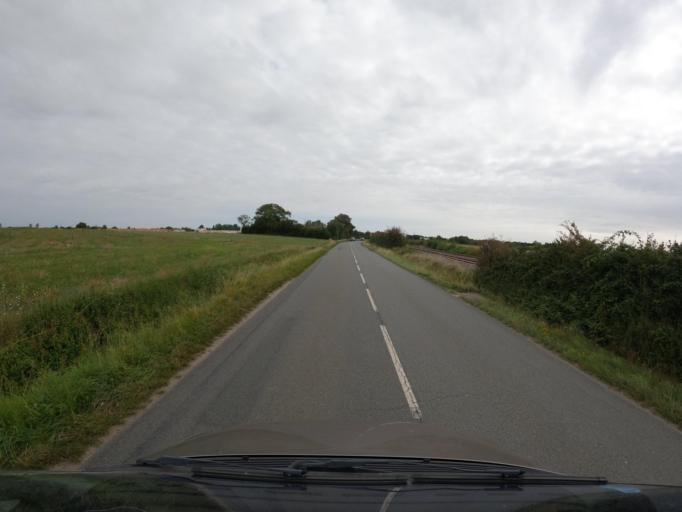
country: FR
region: Poitou-Charentes
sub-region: Departement de la Charente-Maritime
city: Marans
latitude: 46.3049
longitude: -1.0124
